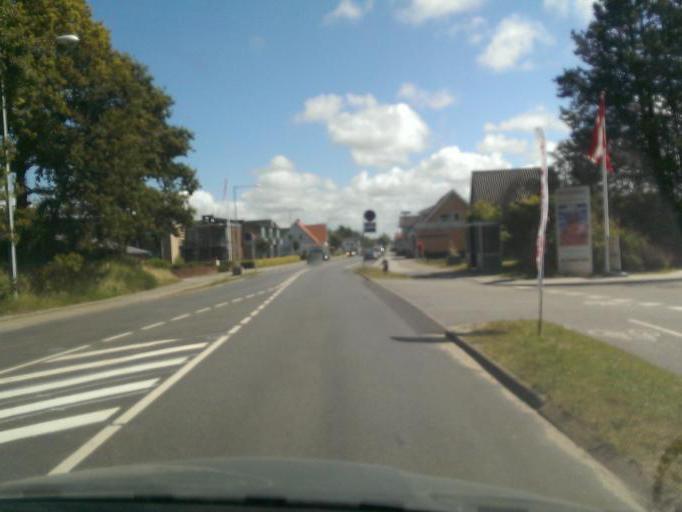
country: DK
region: North Denmark
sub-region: Jammerbugt Kommune
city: Pandrup
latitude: 57.2489
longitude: 9.6122
